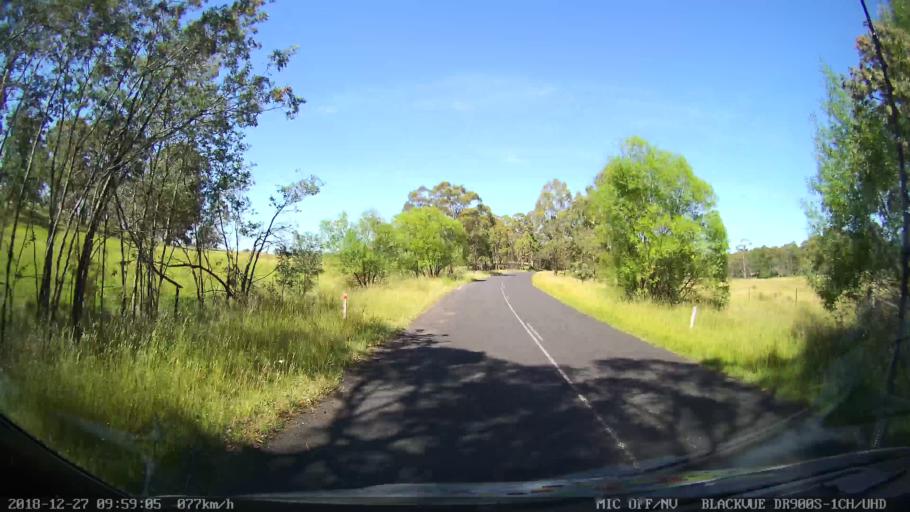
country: AU
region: New South Wales
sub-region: Lithgow
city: Portland
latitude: -33.4325
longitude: 149.9562
